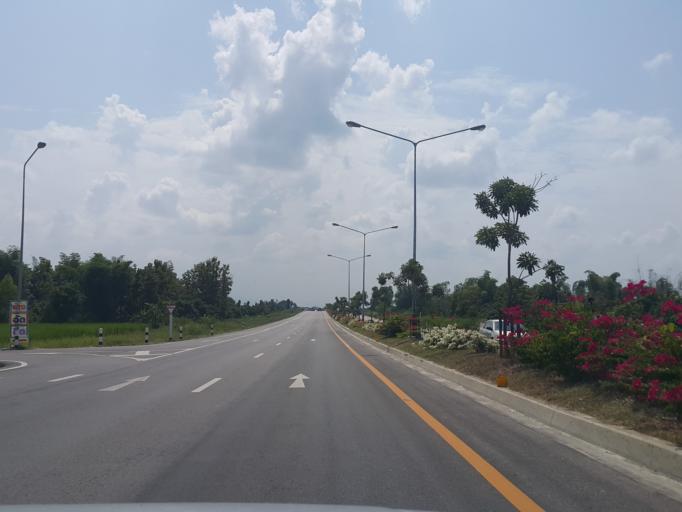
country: TH
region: Chiang Mai
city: San Pa Tong
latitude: 18.5624
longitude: 98.8502
